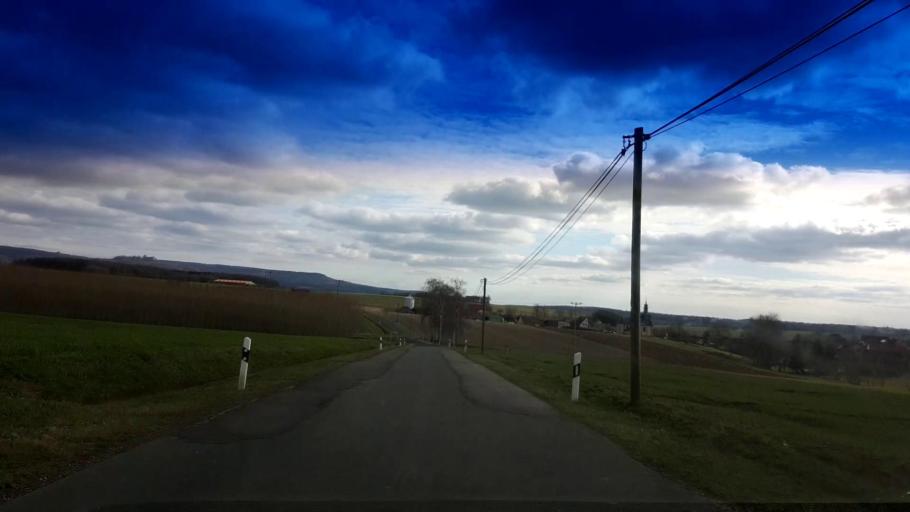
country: DE
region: Bavaria
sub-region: Upper Franconia
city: Schesslitz
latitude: 50.0085
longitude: 11.0204
